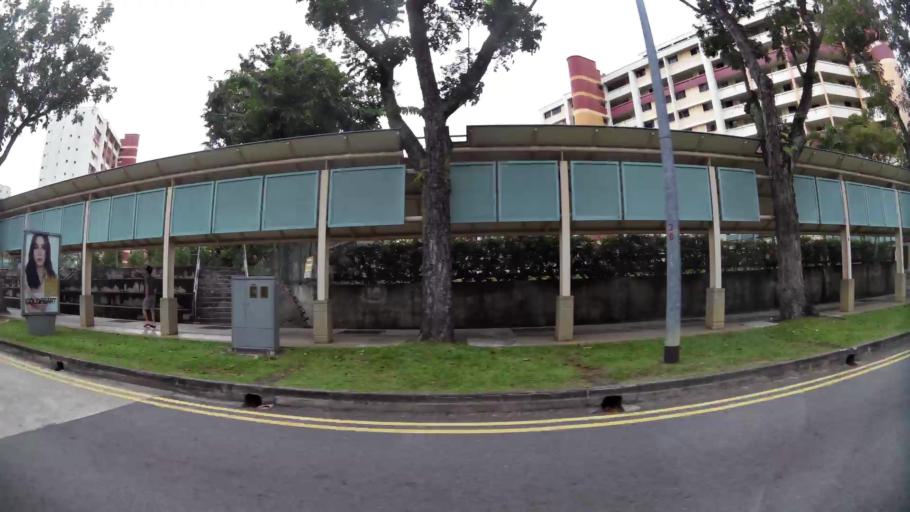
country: SG
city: Singapore
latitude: 1.3542
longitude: 103.8897
